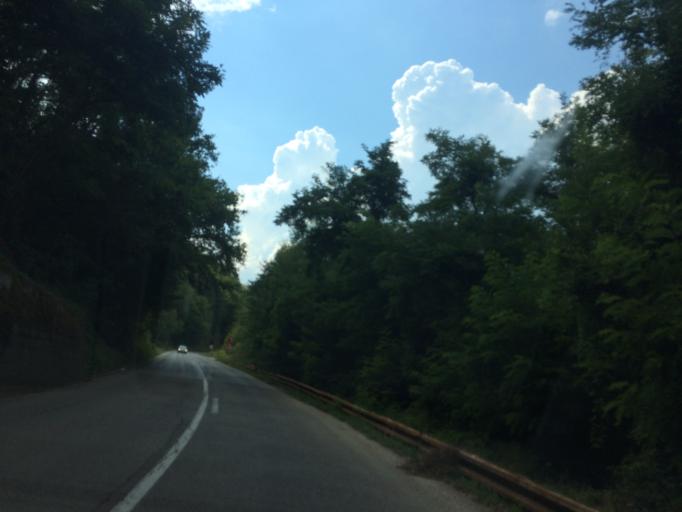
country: RS
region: Central Serbia
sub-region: Zlatiborski Okrug
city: Prijepolje
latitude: 43.3619
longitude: 19.6085
